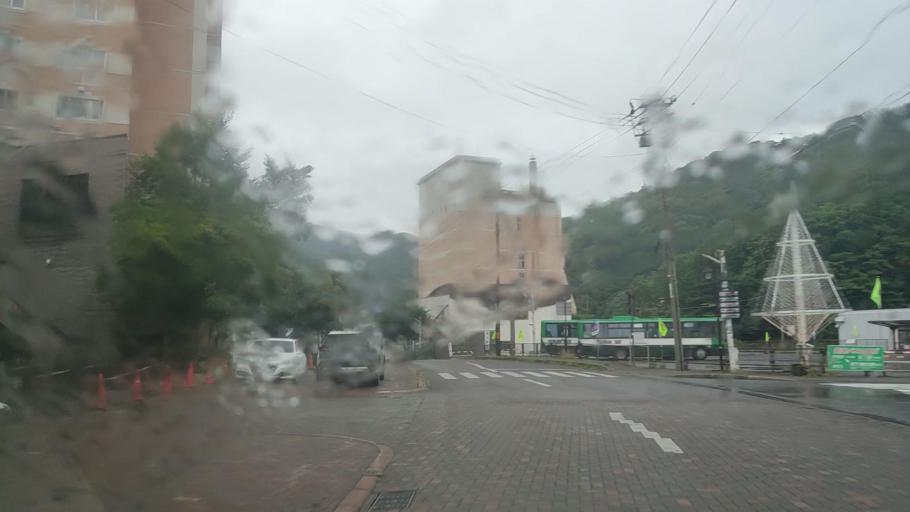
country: JP
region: Hokkaido
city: Shiraoi
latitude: 42.4918
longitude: 141.1434
